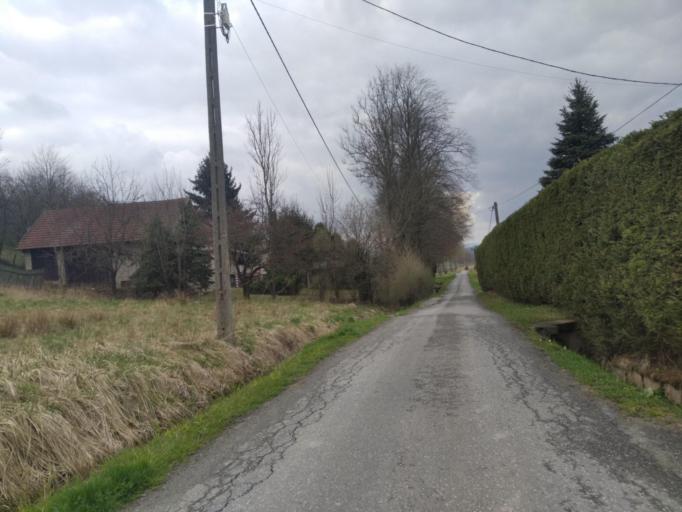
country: PL
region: Subcarpathian Voivodeship
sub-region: Powiat strzyzowski
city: Wisniowa
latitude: 49.8796
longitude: 21.7052
